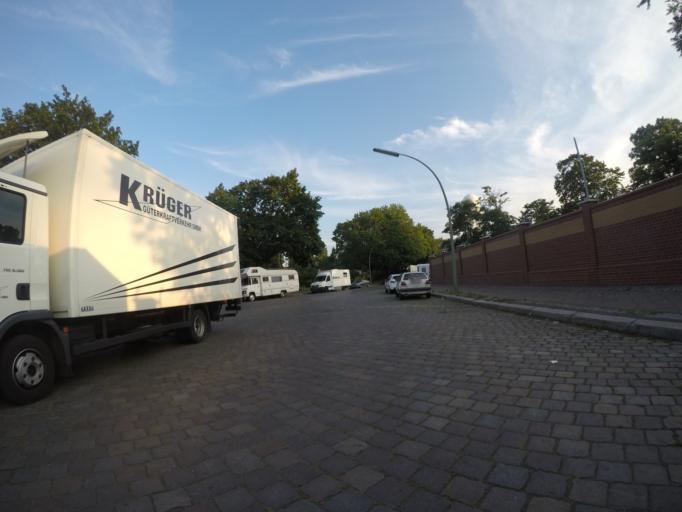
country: DE
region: Berlin
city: Bezirk Kreuzberg
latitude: 52.4851
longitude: 13.4013
